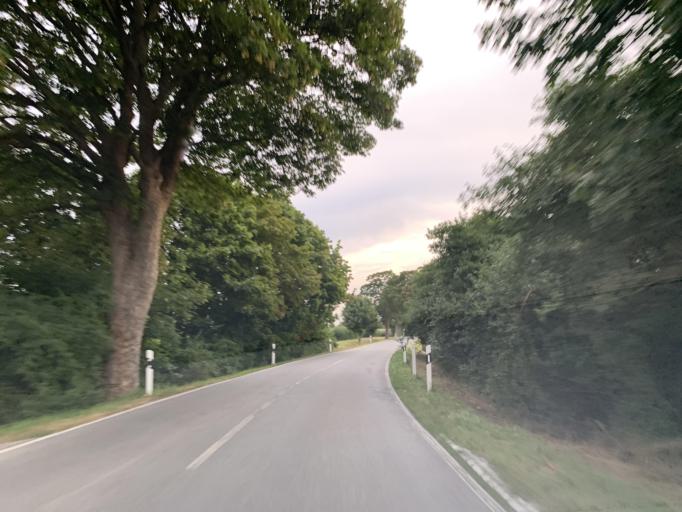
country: DE
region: Mecklenburg-Vorpommern
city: Neverin
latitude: 53.6095
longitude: 13.3293
